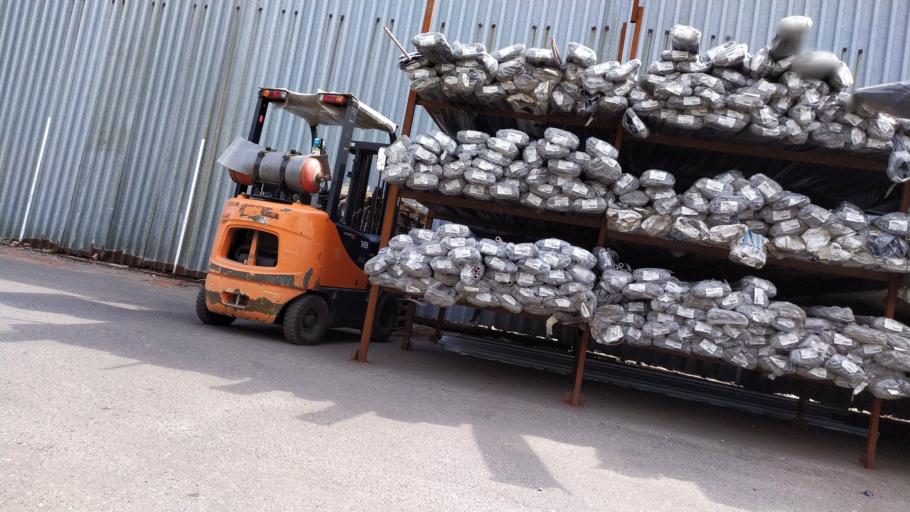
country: RU
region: Kursk
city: Kursk
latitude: 51.6574
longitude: 36.1377
